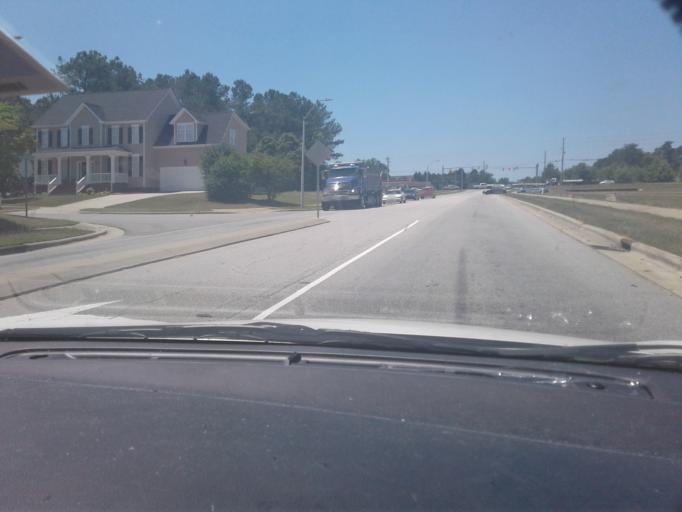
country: US
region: North Carolina
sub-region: Wake County
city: Fuquay-Varina
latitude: 35.6034
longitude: -78.8009
